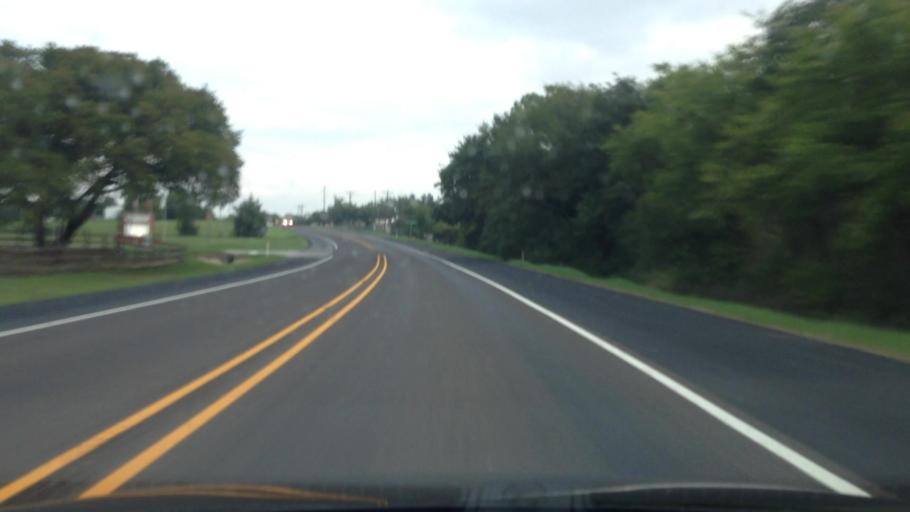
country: US
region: Texas
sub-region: Johnson County
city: Burleson
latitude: 32.4883
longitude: -97.3363
